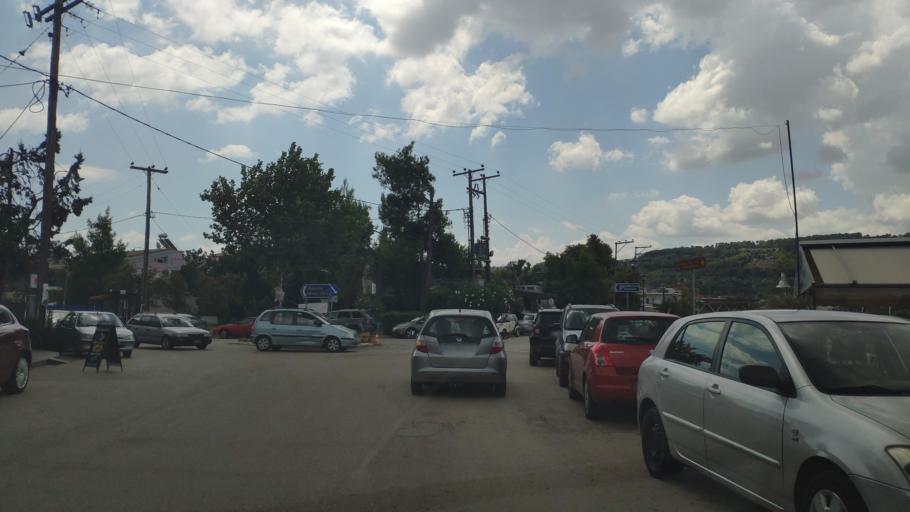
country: GR
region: Central Greece
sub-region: Nomos Fthiotidos
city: Malesina
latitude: 38.6563
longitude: 23.1921
